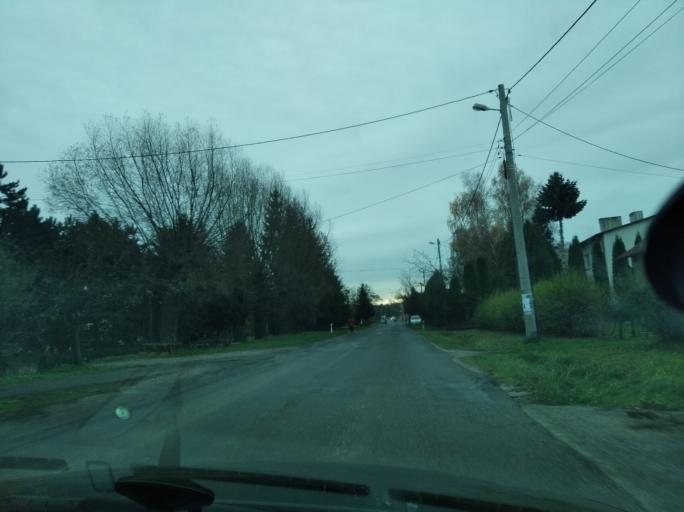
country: PL
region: Subcarpathian Voivodeship
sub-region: Powiat lancucki
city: Krzemienica
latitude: 50.0845
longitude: 22.1879
